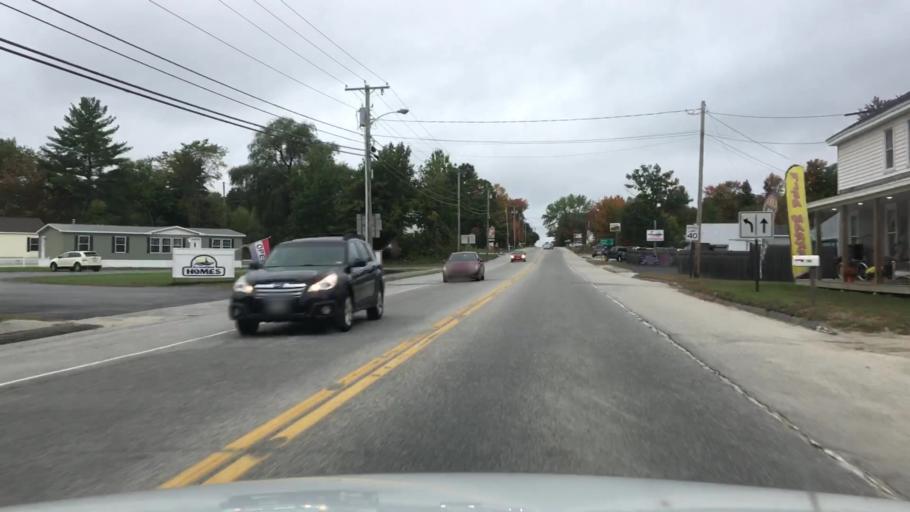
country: US
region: Maine
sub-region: Oxford County
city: Oxford
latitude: 44.1346
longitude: -70.4652
